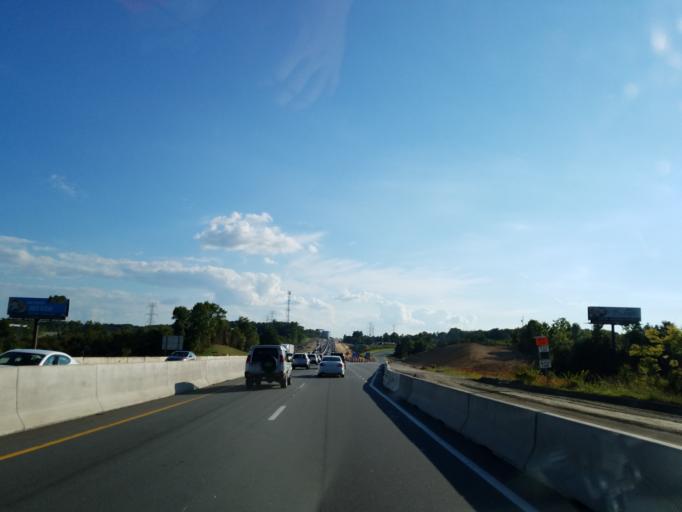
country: US
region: North Carolina
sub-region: Cabarrus County
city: Kannapolis
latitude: 35.4612
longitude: -80.5901
